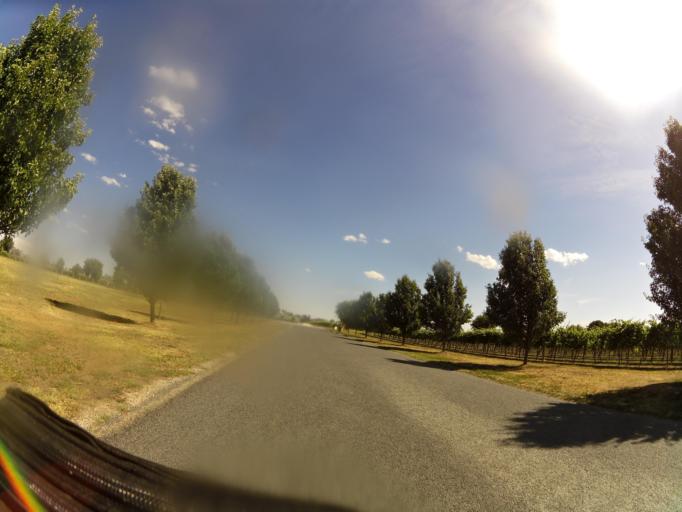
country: AU
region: Victoria
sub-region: Campaspe
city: Kyabram
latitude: -36.8527
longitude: 145.0899
